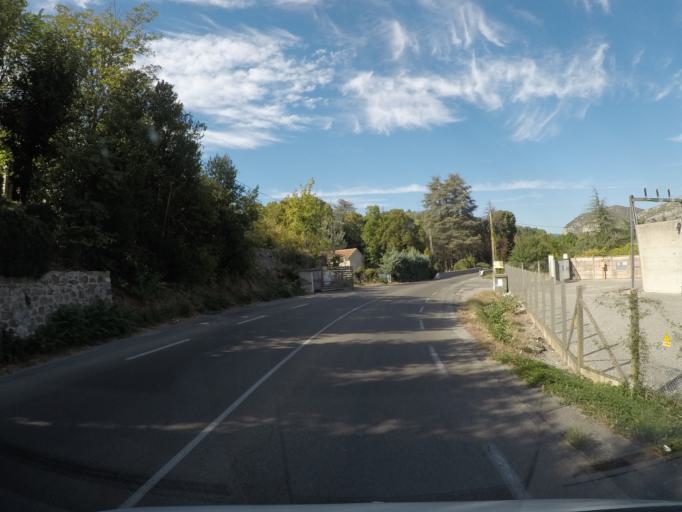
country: FR
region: Languedoc-Roussillon
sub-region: Departement du Gard
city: Anduze
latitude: 44.0414
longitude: 3.9849
